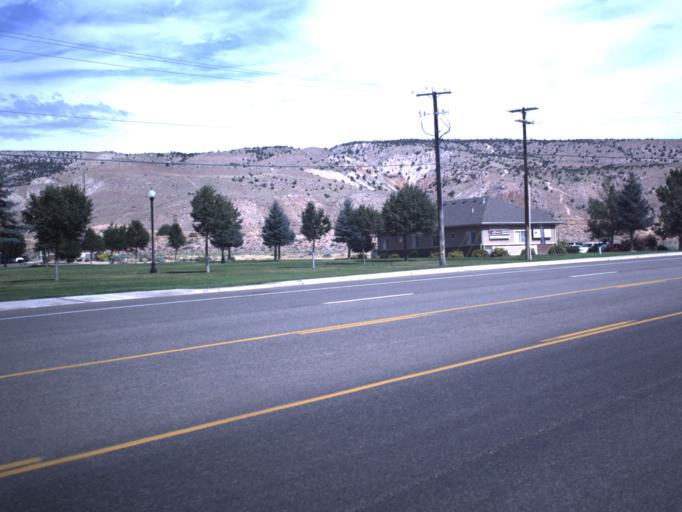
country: US
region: Utah
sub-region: Sevier County
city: Richfield
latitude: 38.7828
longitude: -112.0847
